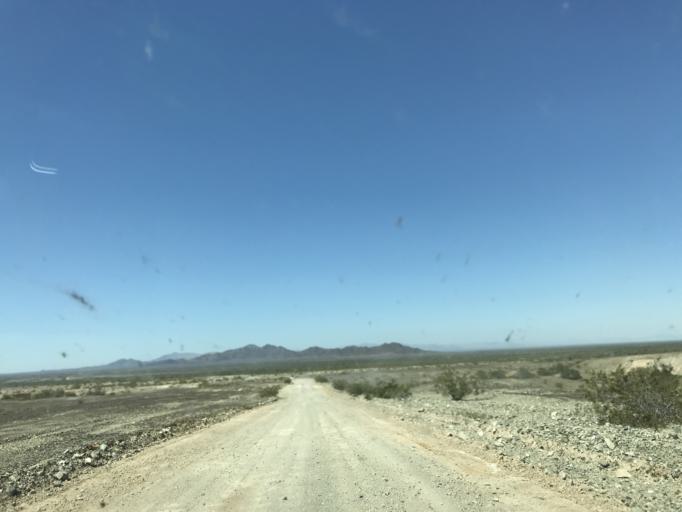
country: US
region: California
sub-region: Riverside County
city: Mesa Verde
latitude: 33.5006
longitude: -114.8562
